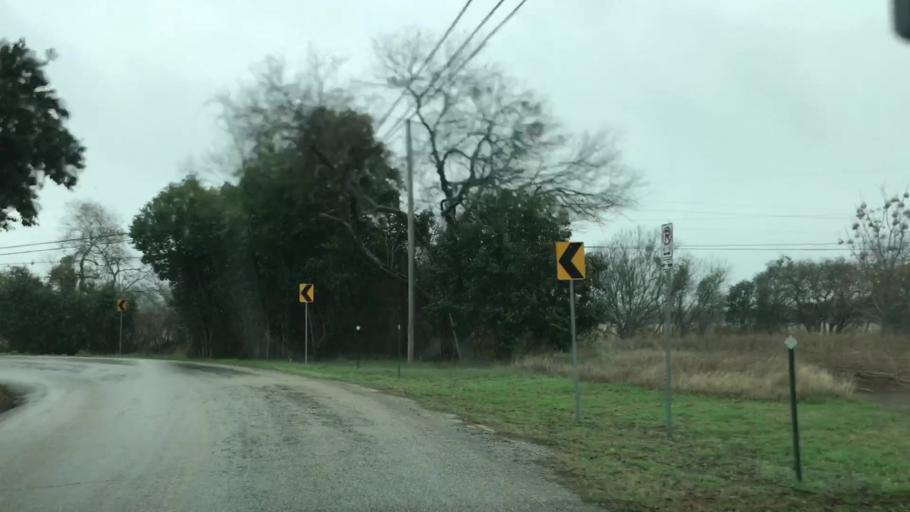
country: US
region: Texas
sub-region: Hays County
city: San Marcos
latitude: 29.8944
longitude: -97.8983
